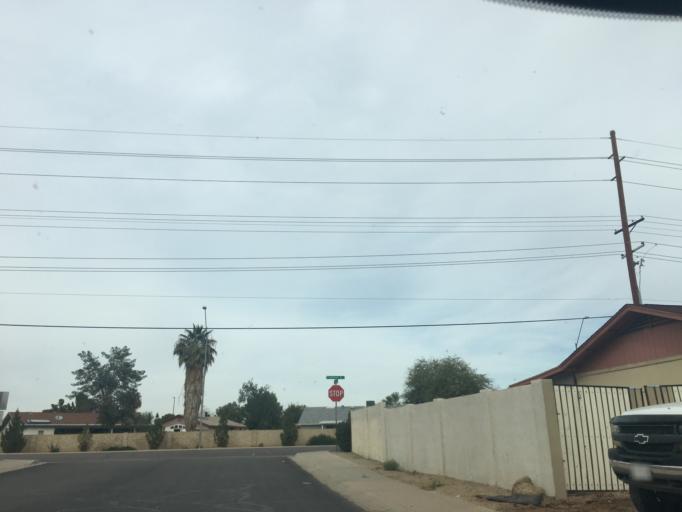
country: US
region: Arizona
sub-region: Maricopa County
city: Gilbert
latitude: 33.3640
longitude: -111.7954
